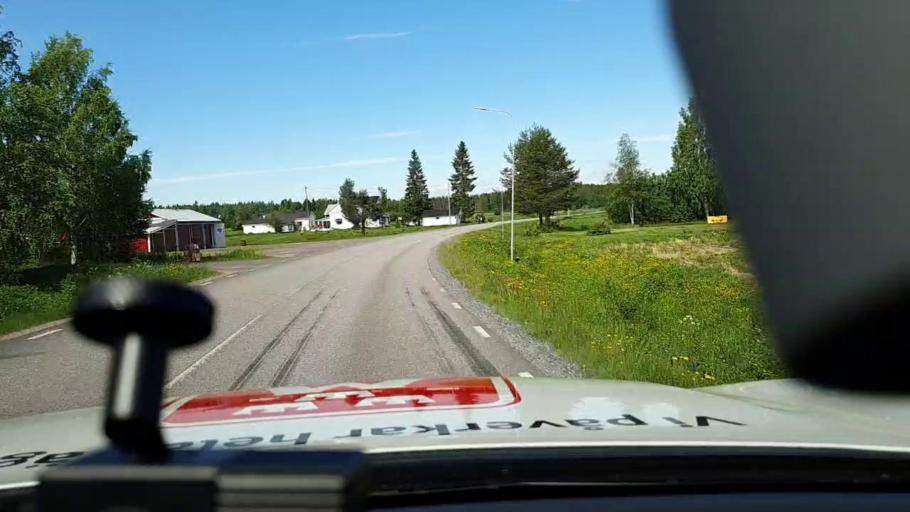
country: SE
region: Norrbotten
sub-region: Lulea Kommun
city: Sodra Sunderbyn
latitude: 65.6604
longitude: 21.8304
